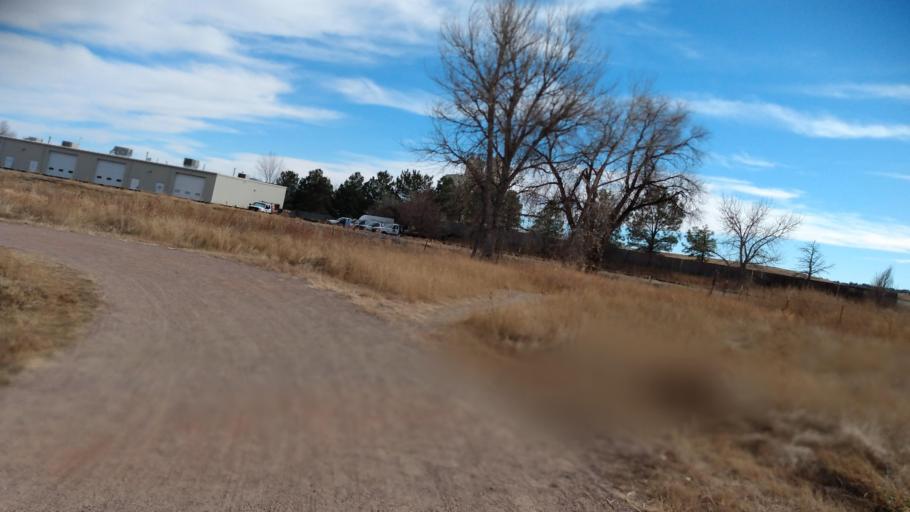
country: US
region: Colorado
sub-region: Boulder County
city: Lafayette
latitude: 39.9799
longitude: -105.0764
